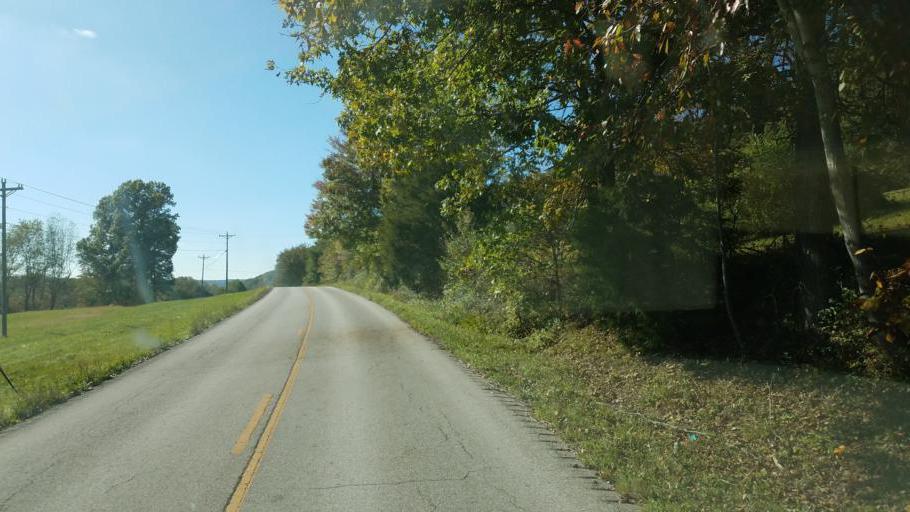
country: US
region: Kentucky
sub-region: Fleming County
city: Flemingsburg
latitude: 38.4687
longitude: -83.5537
